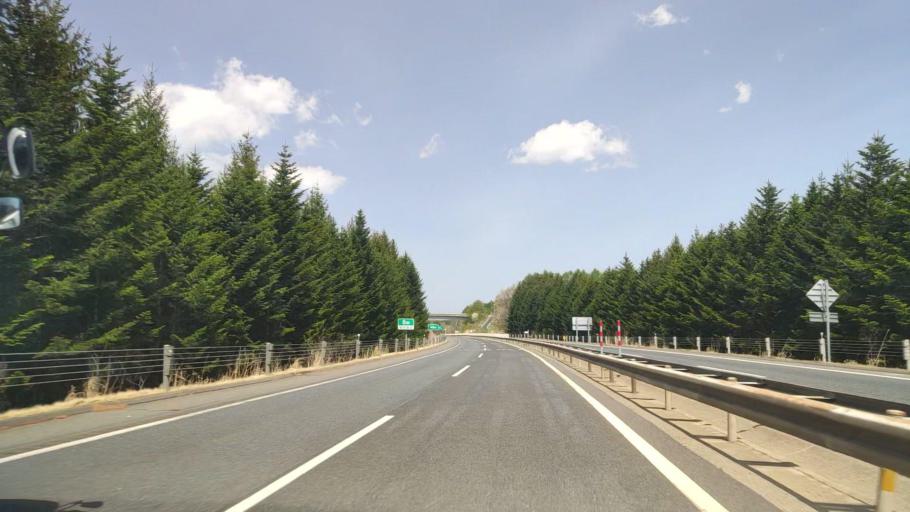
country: JP
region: Aomori
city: Hachinohe
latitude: 40.4129
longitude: 141.4434
